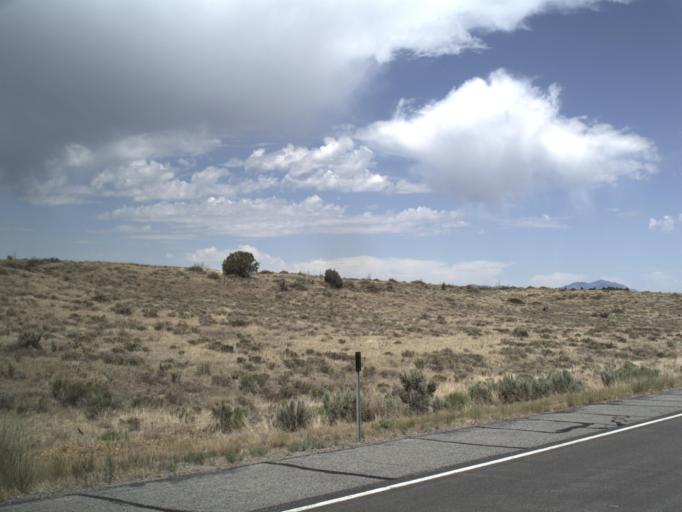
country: US
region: Utah
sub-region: Utah County
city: Genola
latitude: 39.9770
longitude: -112.2596
